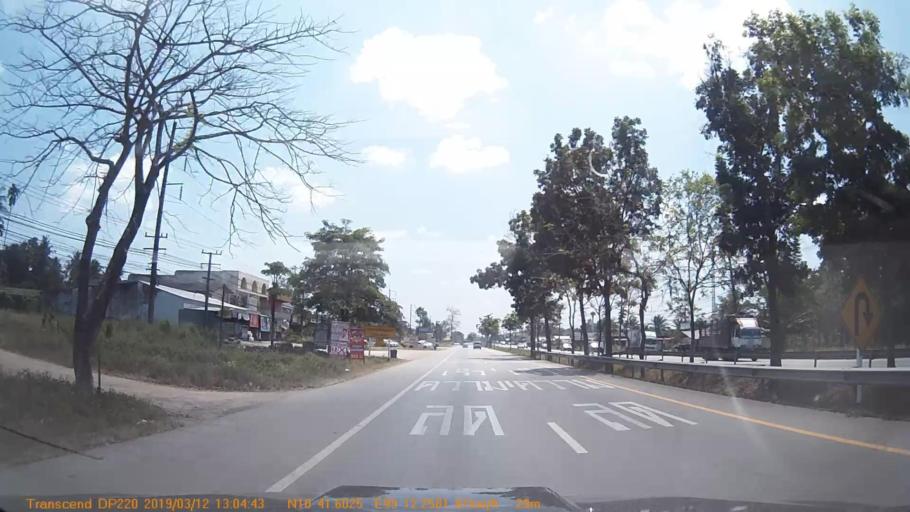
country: TH
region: Chumphon
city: Tha Sae
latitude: 10.6930
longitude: 99.2043
